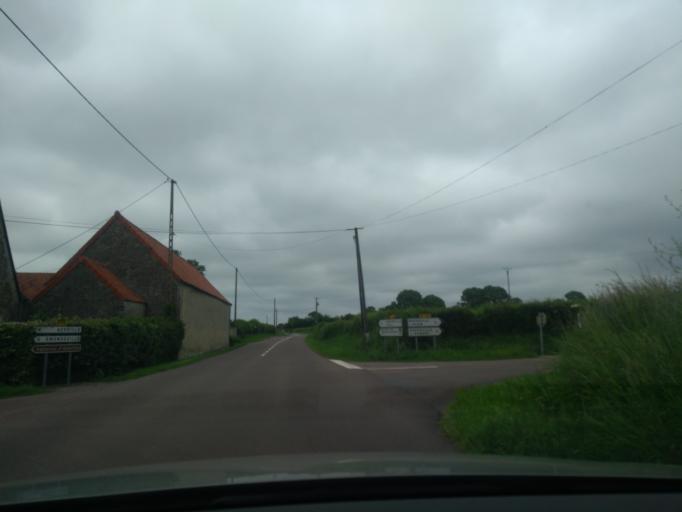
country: FR
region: Lower Normandy
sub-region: Departement de la Manche
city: Sainte-Mere-Eglise
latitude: 49.4307
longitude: -1.3014
